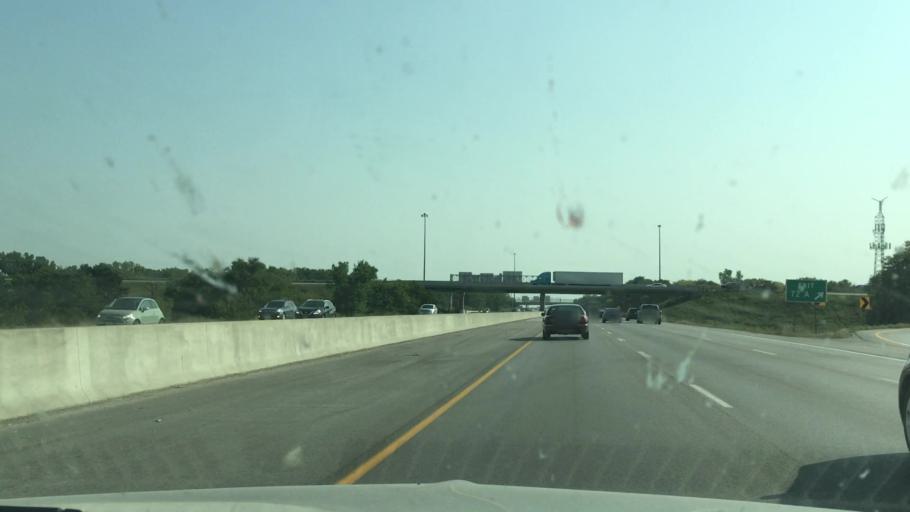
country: US
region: Iowa
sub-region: Polk County
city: Clive
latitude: 41.5914
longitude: -93.7774
